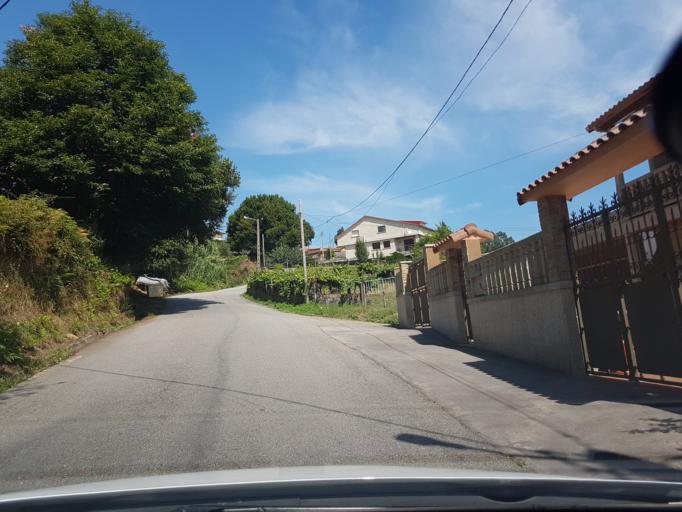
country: ES
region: Galicia
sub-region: Provincia de Pontevedra
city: Porrino
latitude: 42.2173
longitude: -8.6299
